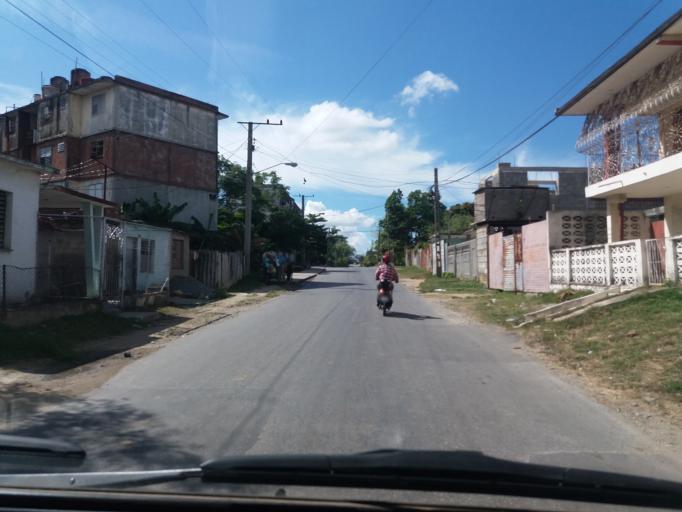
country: CU
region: Cienfuegos
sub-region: Municipio de Cienfuegos
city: Cienfuegos
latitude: 22.1506
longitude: -80.4277
